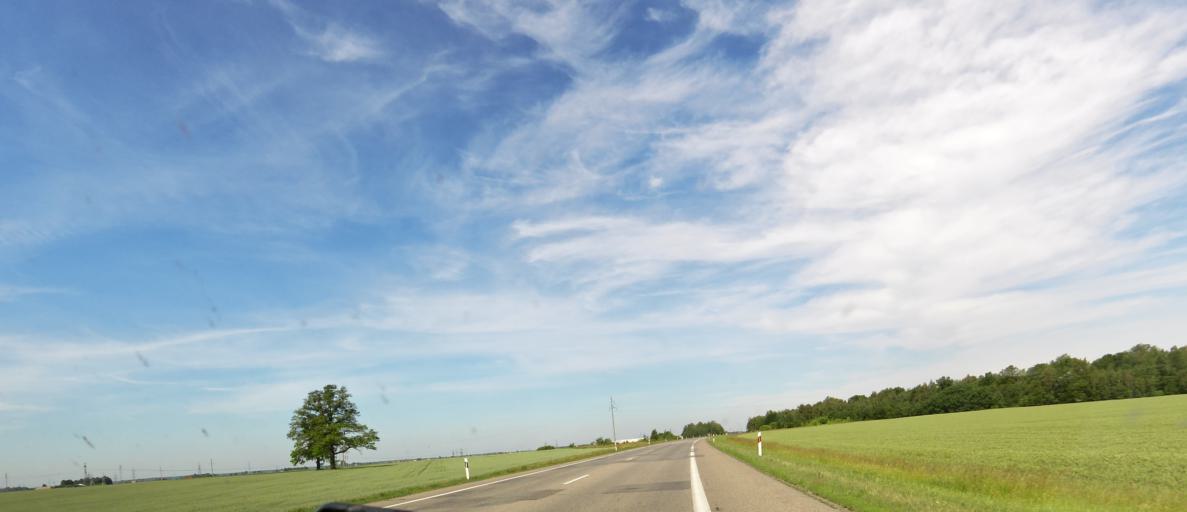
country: LT
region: Panevezys
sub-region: Panevezys City
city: Panevezys
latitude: 55.6793
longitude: 24.3049
